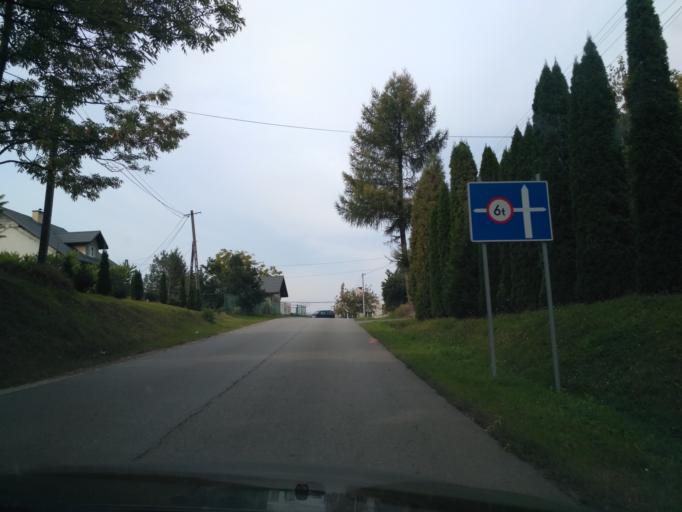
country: PL
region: Subcarpathian Voivodeship
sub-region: Powiat rzeszowski
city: Trzciana
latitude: 50.0491
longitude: 21.8313
